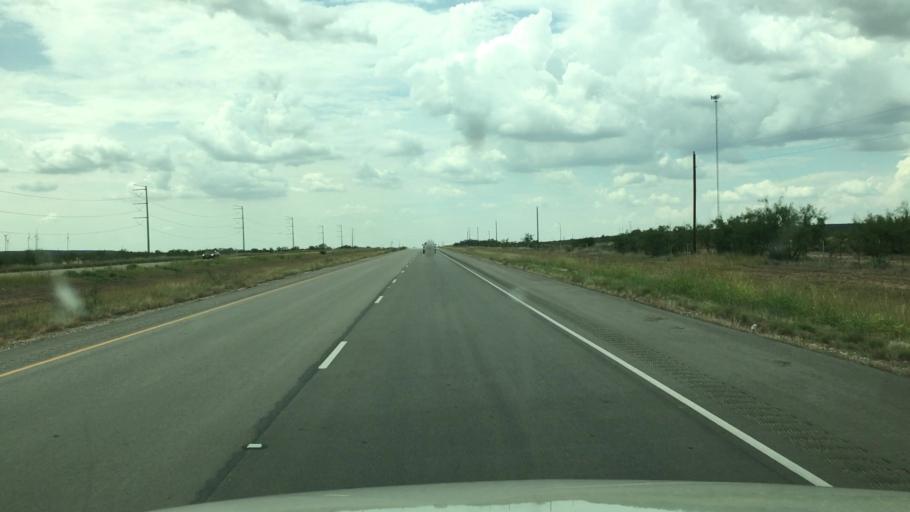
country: US
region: Texas
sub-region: Glasscock County
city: Garden City
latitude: 31.9772
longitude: -101.2502
